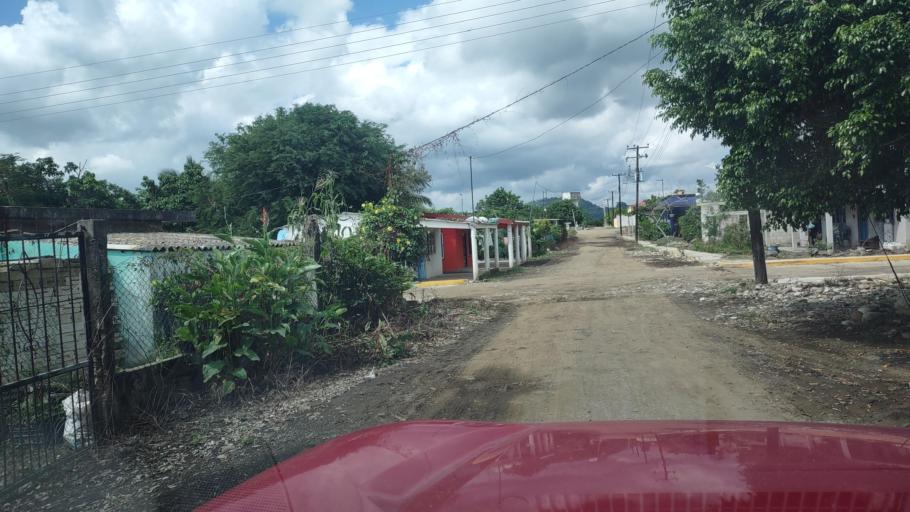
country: MX
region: Puebla
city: San Jose Acateno
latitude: 20.2746
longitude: -97.1287
